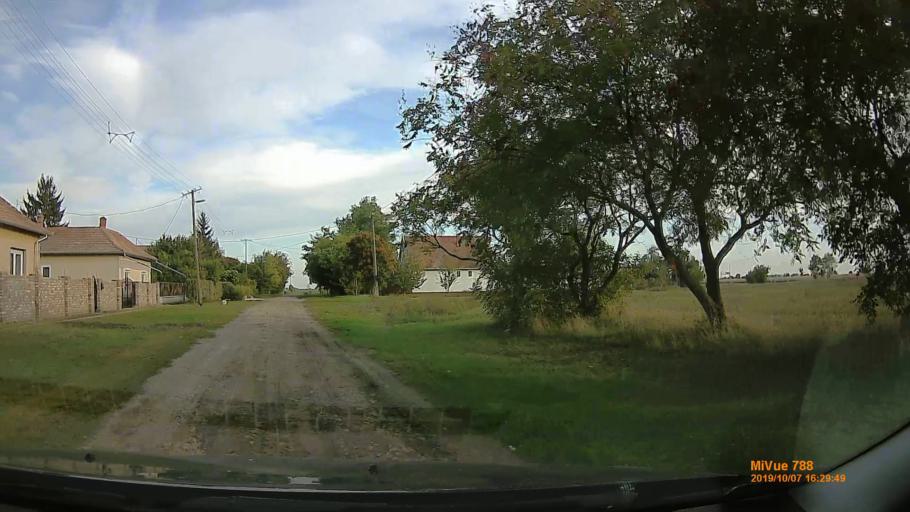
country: HU
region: Bekes
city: Szarvas
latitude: 46.8184
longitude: 20.6526
